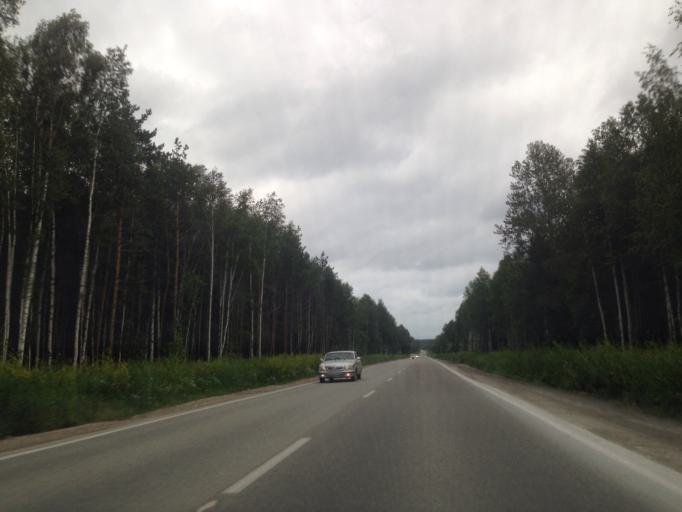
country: RU
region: Sverdlovsk
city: Istok
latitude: 56.8432
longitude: 60.7349
